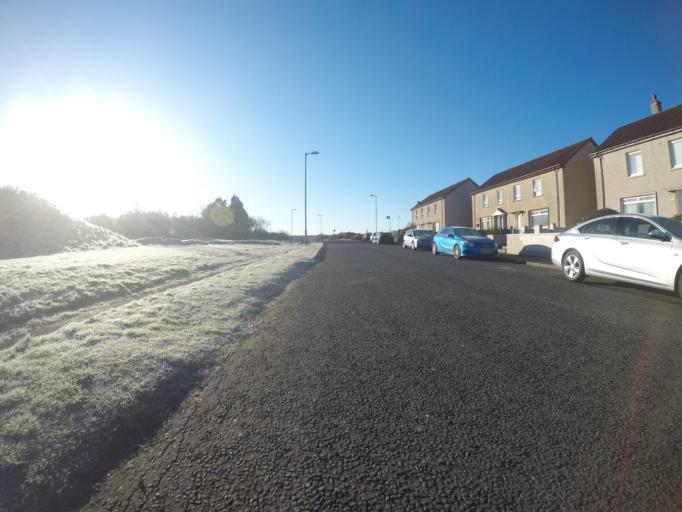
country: GB
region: Scotland
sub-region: North Ayrshire
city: Stevenston
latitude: 55.6304
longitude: -4.7394
